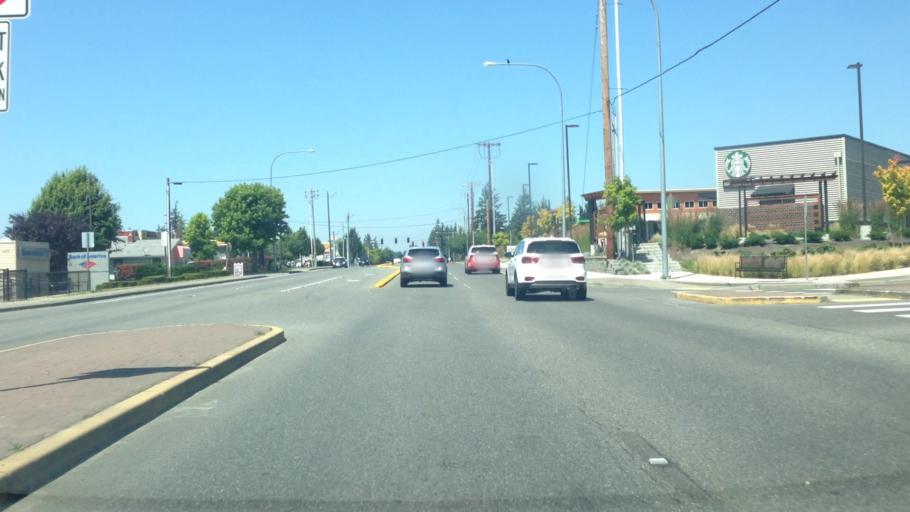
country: US
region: Washington
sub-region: Pierce County
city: Edgewood
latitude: 47.2508
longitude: -122.2938
